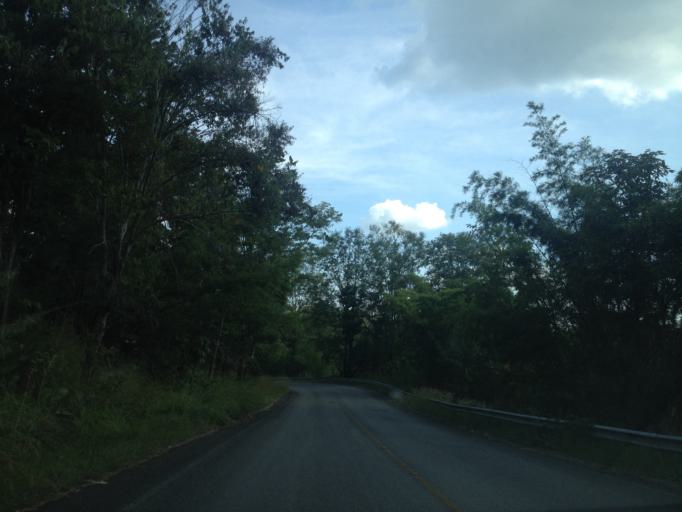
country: TH
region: Chiang Mai
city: Samoeng
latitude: 18.8055
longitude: 98.8108
